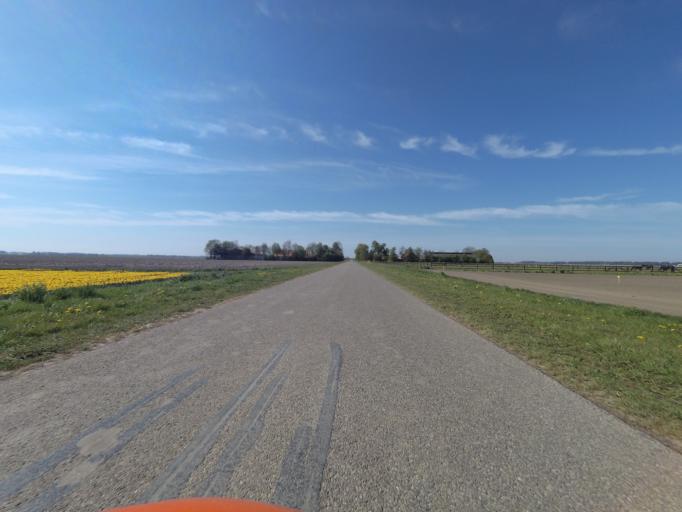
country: NL
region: Flevoland
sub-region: Gemeente Dronten
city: Dronten
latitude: 52.5752
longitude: 5.6984
